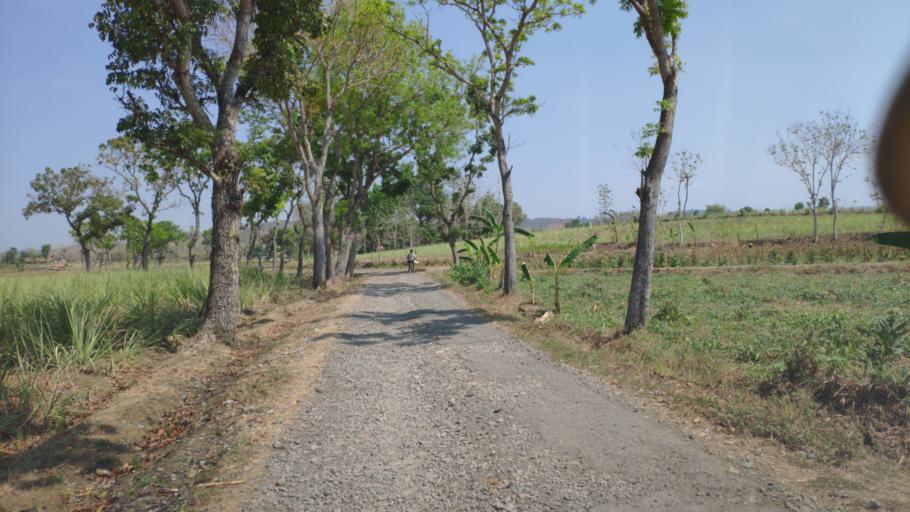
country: ID
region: Central Java
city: Ngundaan
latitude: -6.9189
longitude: 111.3960
